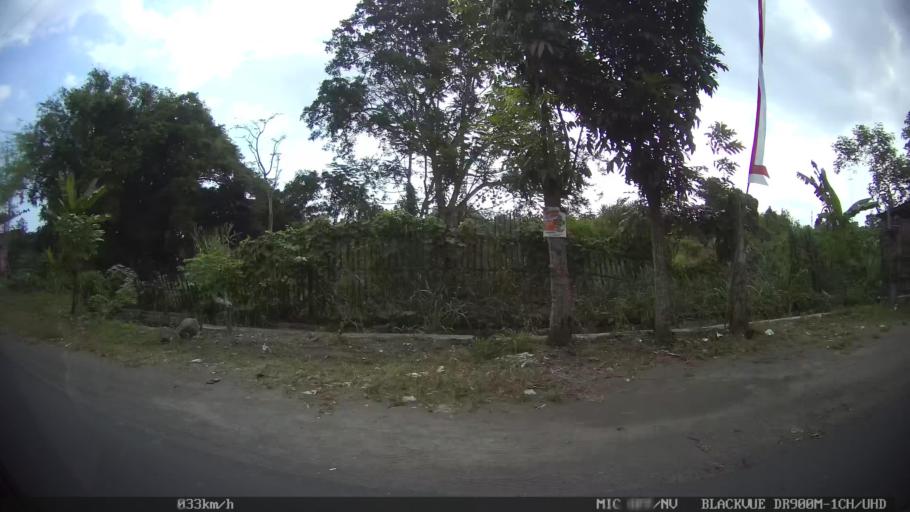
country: ID
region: Daerah Istimewa Yogyakarta
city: Gamping Lor
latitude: -7.7872
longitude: 110.3417
